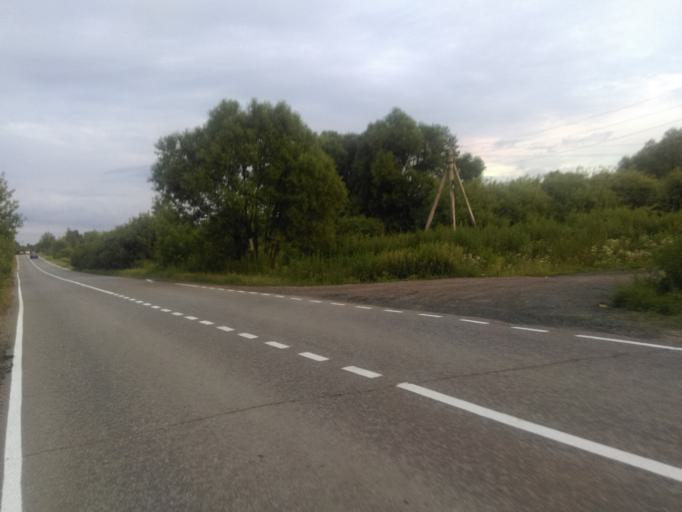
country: RU
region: Moskovskaya
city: Vostryakovo
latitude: 55.3892
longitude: 37.8086
